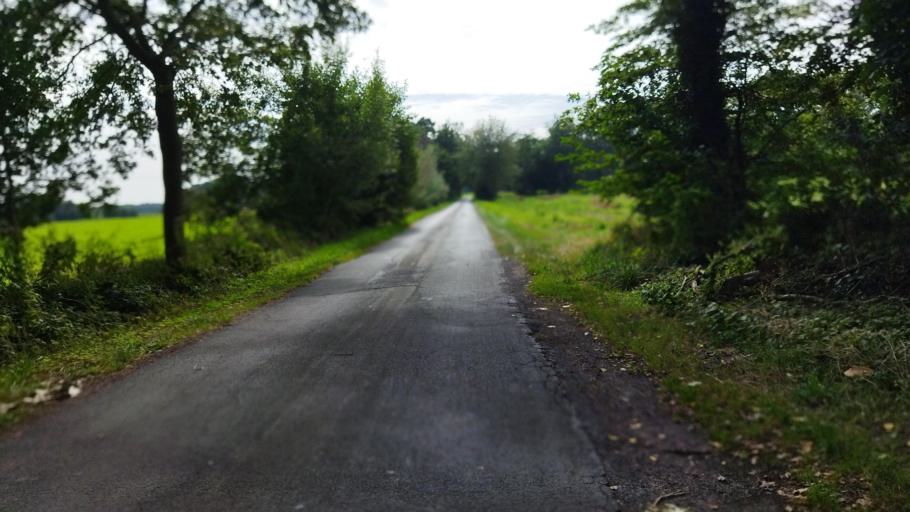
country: DE
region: North Rhine-Westphalia
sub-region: Regierungsbezirk Munster
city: Lienen
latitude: 52.1354
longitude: 7.9991
